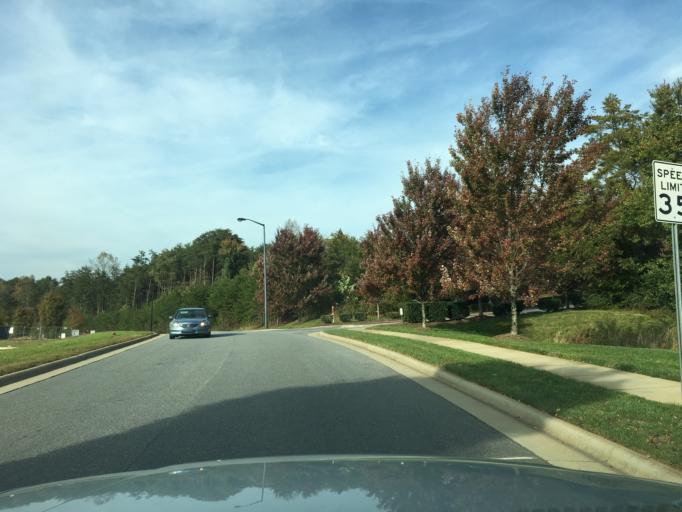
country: US
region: North Carolina
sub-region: Catawba County
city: Saint Stephens
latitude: 35.7288
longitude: -81.2870
